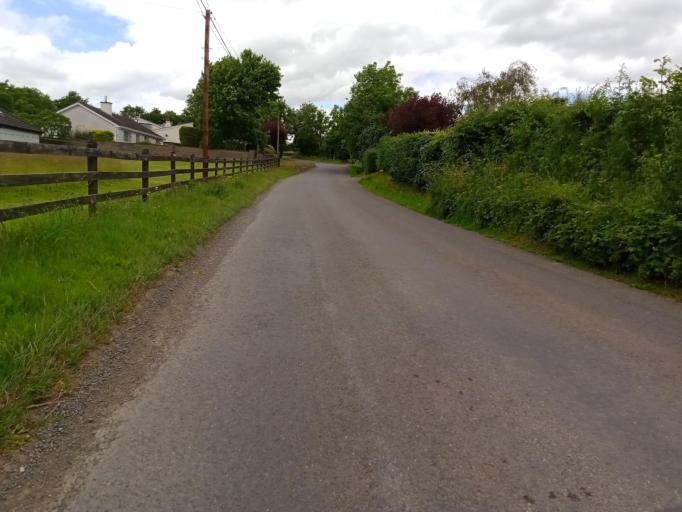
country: IE
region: Leinster
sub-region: Kilkenny
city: Kilkenny
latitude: 52.6917
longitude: -7.2494
